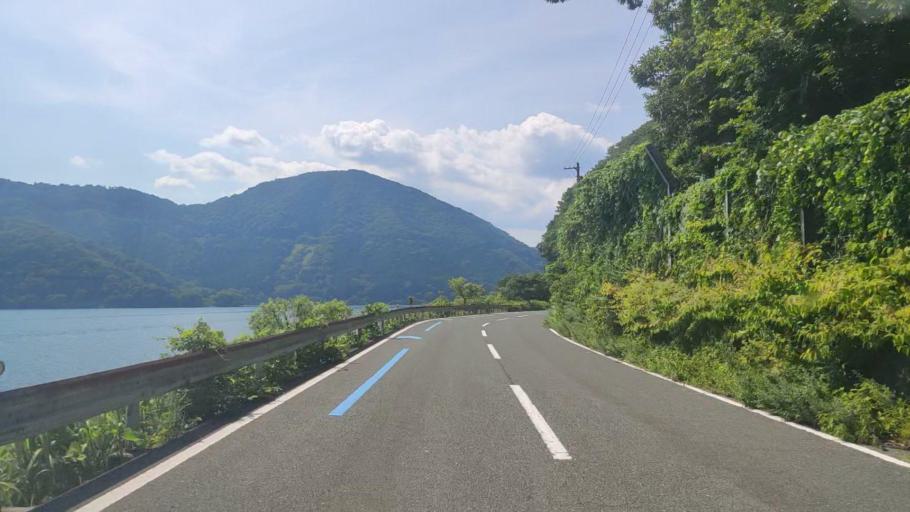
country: JP
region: Shiga Prefecture
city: Nagahama
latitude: 35.5006
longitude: 136.1728
